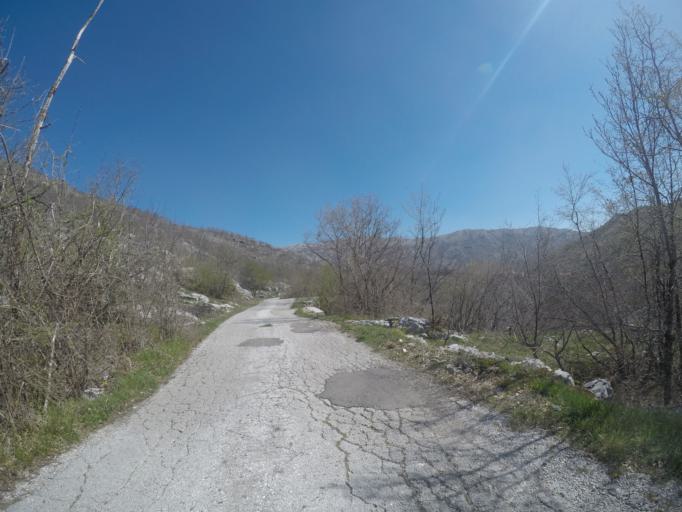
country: ME
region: Cetinje
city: Cetinje
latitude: 42.5359
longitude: 18.9799
